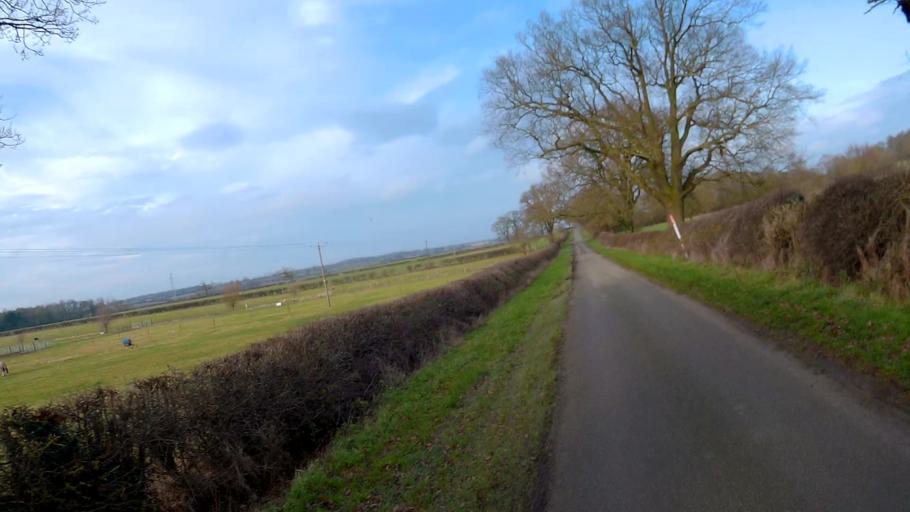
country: GB
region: England
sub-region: Lincolnshire
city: Bourne
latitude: 52.7633
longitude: -0.4197
